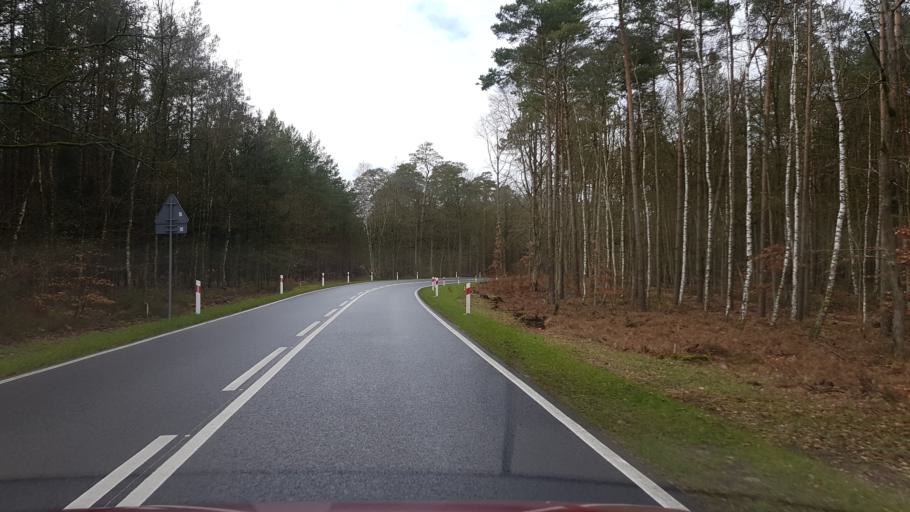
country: PL
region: West Pomeranian Voivodeship
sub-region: Powiat policki
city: Nowe Warpno
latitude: 53.6675
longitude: 14.4223
